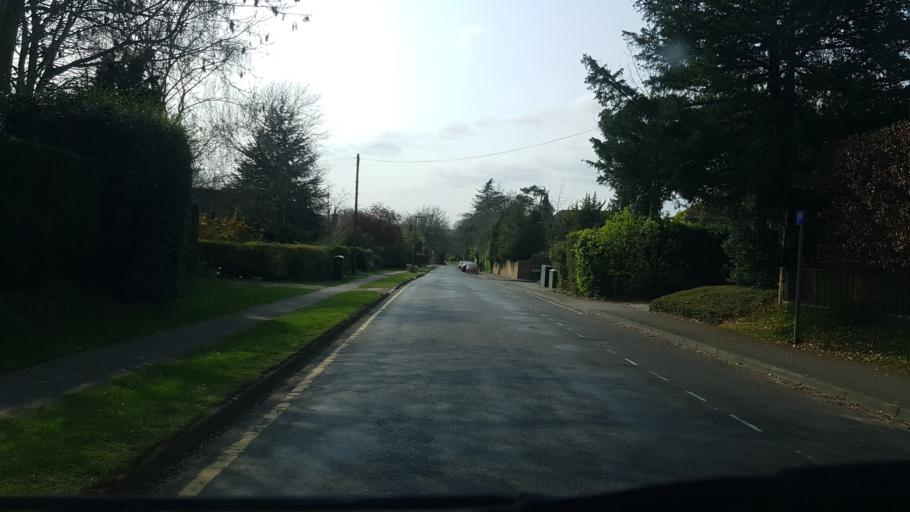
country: GB
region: England
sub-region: Surrey
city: Chilworth
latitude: 51.2364
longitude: -0.5463
